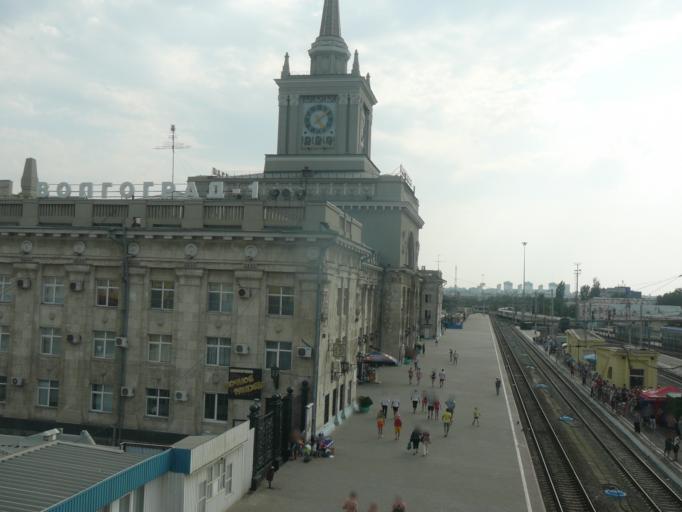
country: RU
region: Volgograd
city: Volgograd
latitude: 48.7133
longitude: 44.5144
